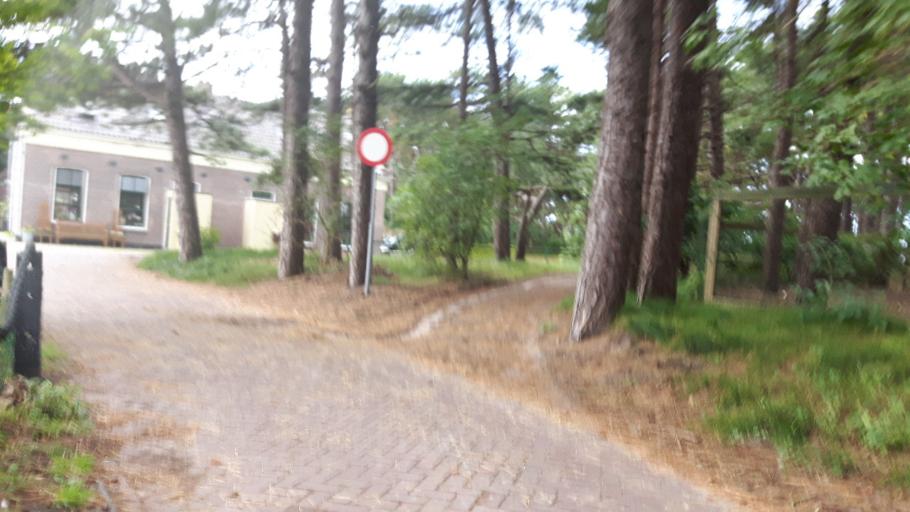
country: NL
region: Friesland
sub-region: Gemeente Ameland
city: Hollum
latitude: 53.4486
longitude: 5.6269
